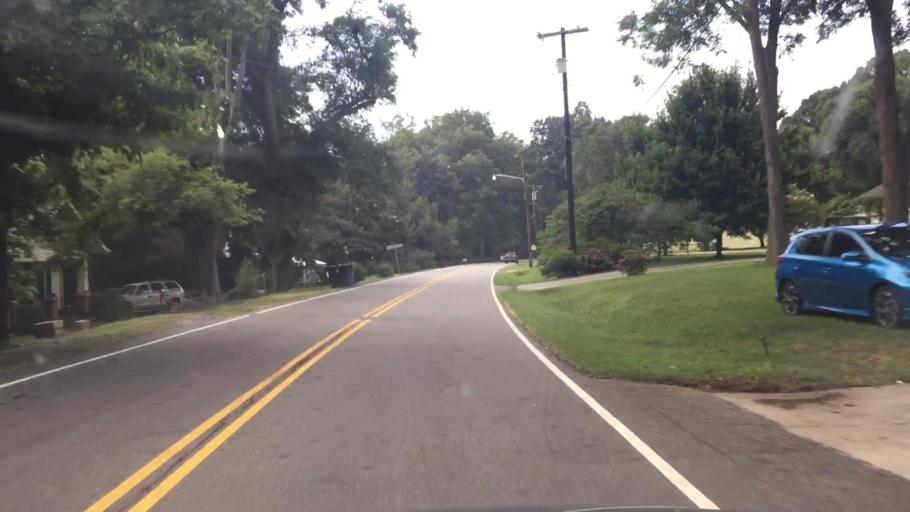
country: US
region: North Carolina
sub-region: Iredell County
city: Mooresville
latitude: 35.5880
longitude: -80.7995
